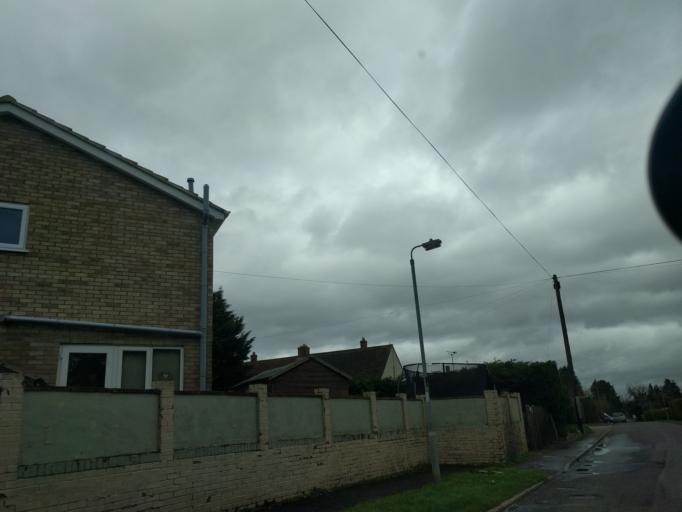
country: GB
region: England
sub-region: Wiltshire
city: Biddestone
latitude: 51.4891
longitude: -2.1934
